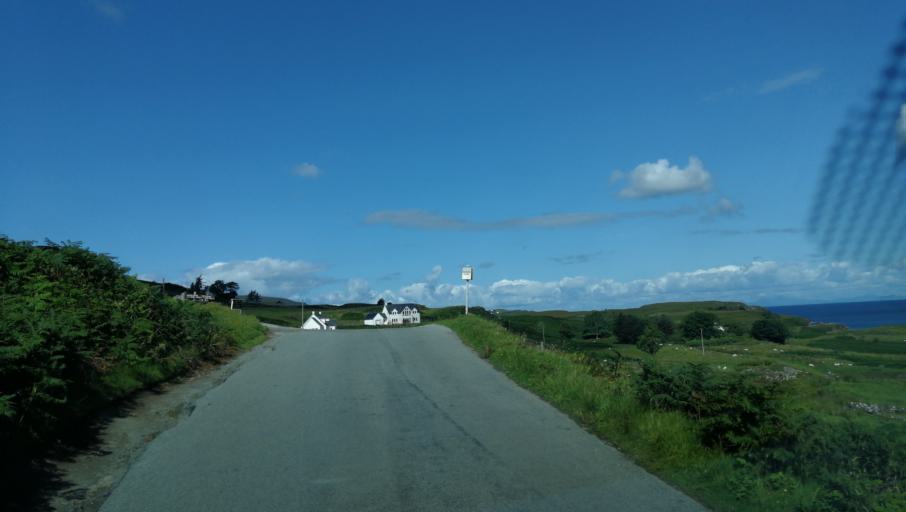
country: GB
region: Scotland
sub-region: Highland
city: Isle of Skye
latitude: 57.4488
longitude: -6.6503
